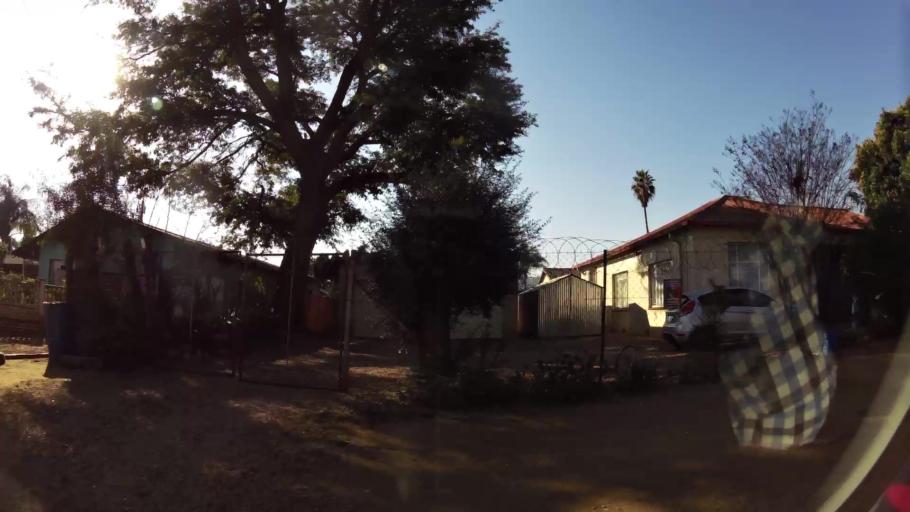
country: ZA
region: Gauteng
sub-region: City of Tshwane Metropolitan Municipality
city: Pretoria
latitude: -25.7133
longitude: 28.1412
